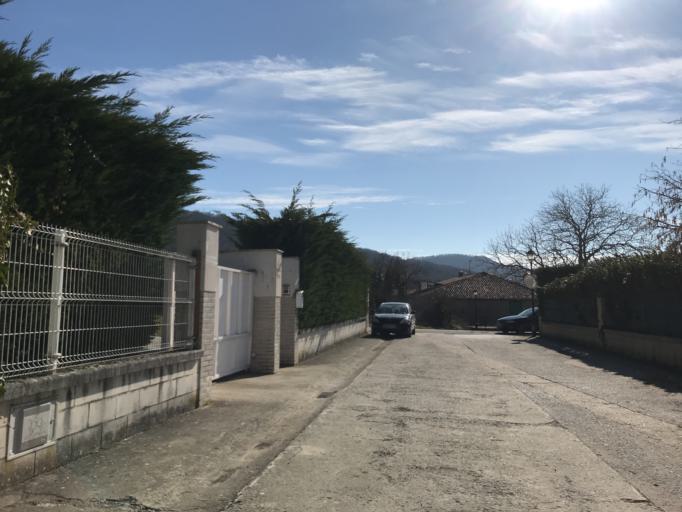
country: ES
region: Basque Country
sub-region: Provincia de Alava
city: Gasteiz / Vitoria
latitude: 42.8061
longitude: -2.6685
